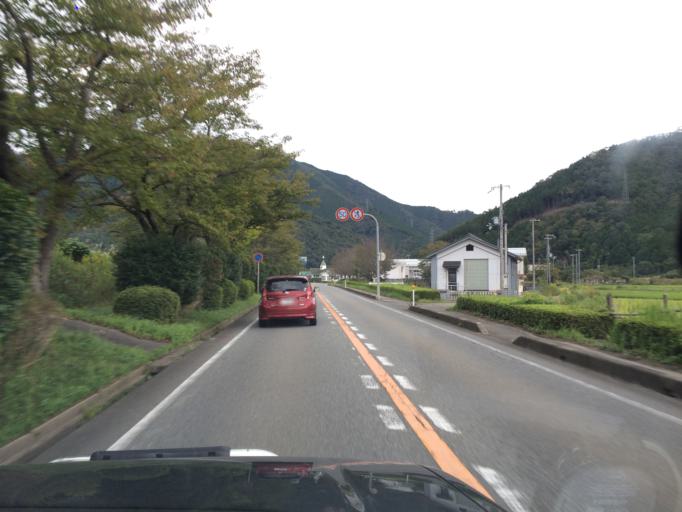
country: JP
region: Hyogo
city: Toyooka
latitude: 35.3801
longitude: 134.8148
